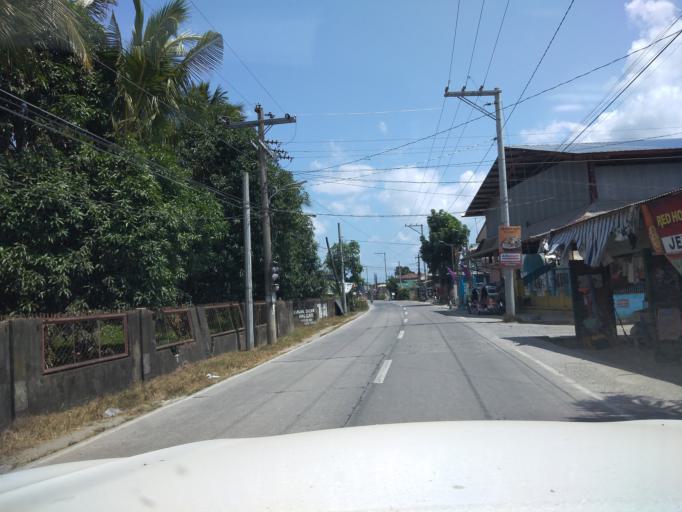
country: PH
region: Central Luzon
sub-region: Province of Pampanga
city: Bahay Pare
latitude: 15.0168
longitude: 120.8713
